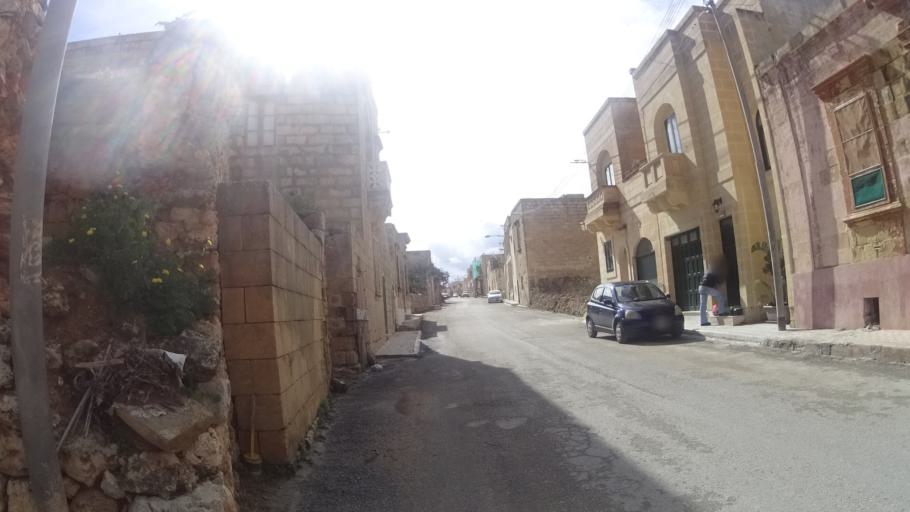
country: MT
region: In-Nadur
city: Nadur
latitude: 36.0474
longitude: 14.2998
